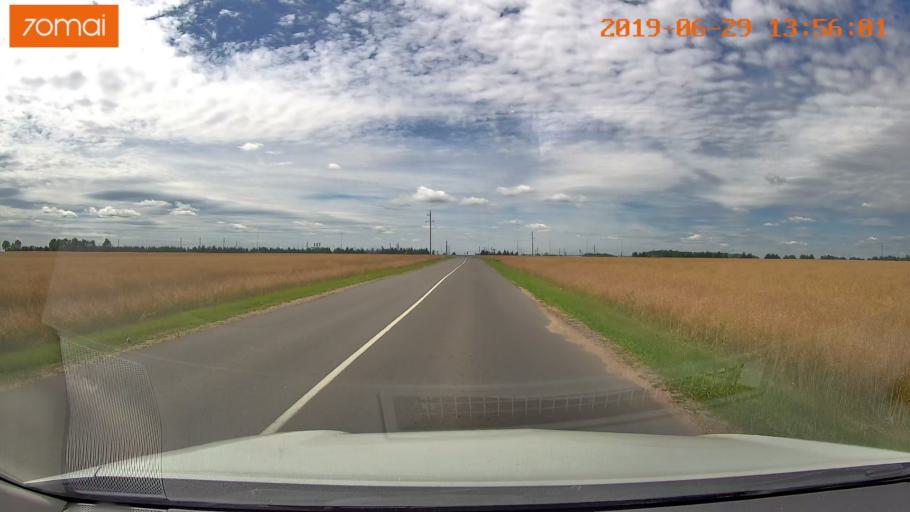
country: BY
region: Minsk
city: Slutsk
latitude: 52.9848
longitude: 27.5110
